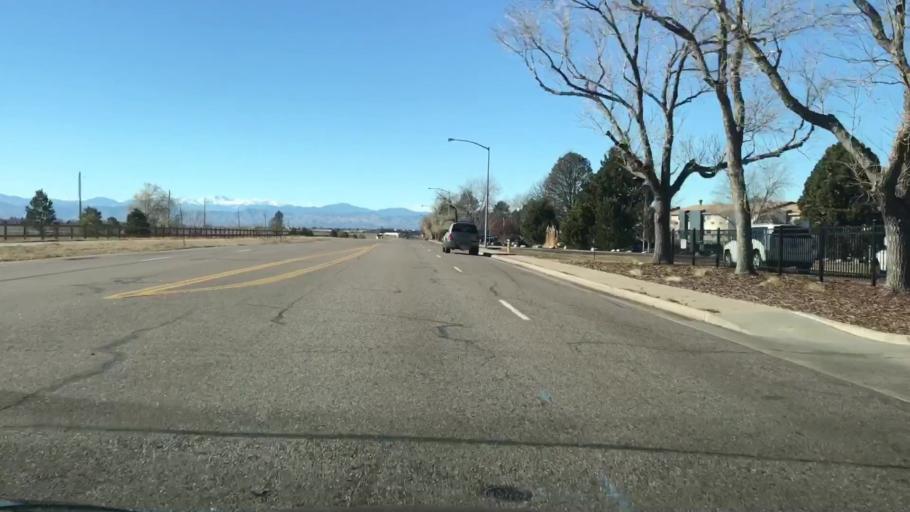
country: US
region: Colorado
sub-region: Adams County
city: Aurora
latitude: 39.7182
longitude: -104.8697
